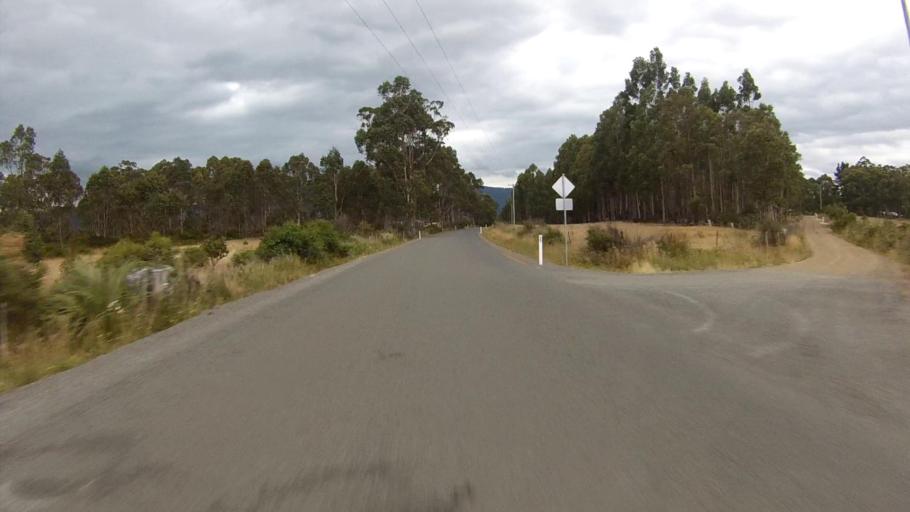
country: AU
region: Tasmania
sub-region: Huon Valley
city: Huonville
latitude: -42.9654
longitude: 147.0841
